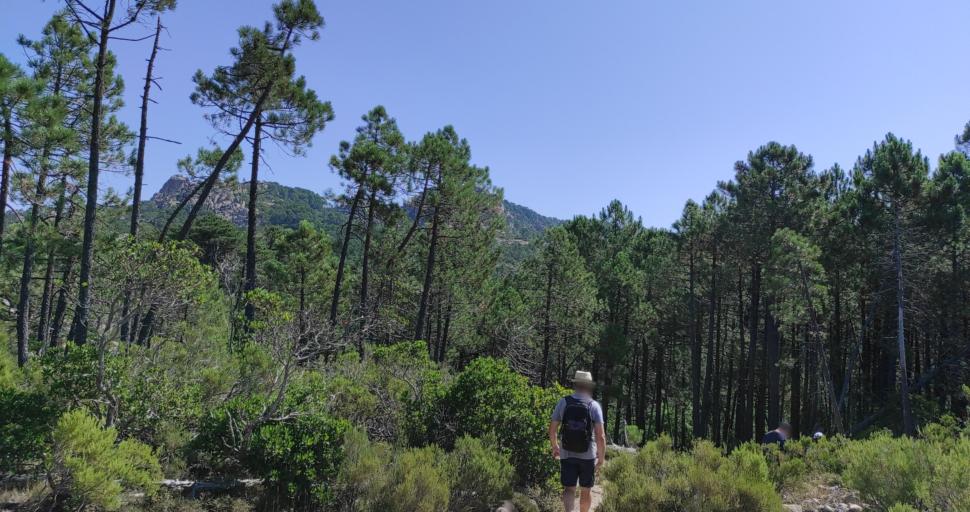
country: FR
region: Corsica
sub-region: Departement de la Corse-du-Sud
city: Zonza
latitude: 41.6836
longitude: 9.2059
